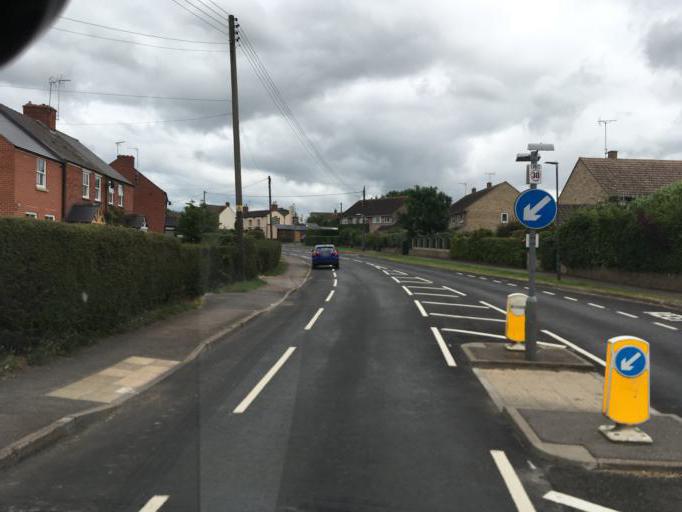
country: GB
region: England
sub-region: Gloucestershire
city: Stonehouse
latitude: 51.7461
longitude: -2.3259
